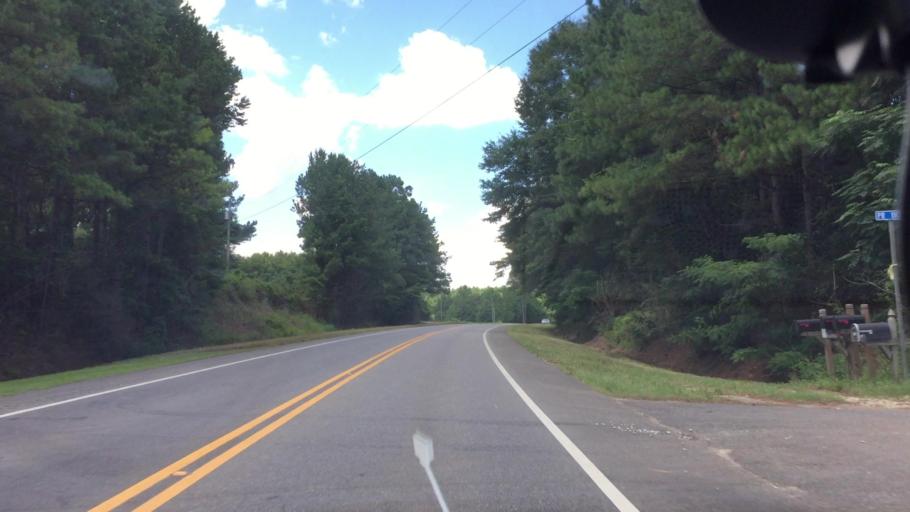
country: US
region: Alabama
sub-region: Pike County
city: Brundidge
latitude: 31.5968
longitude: -85.9463
